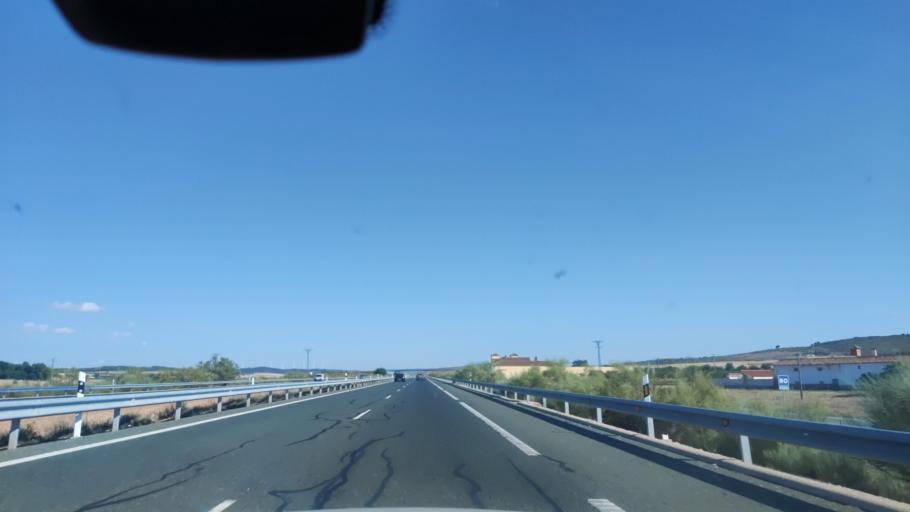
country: ES
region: Castille-La Mancha
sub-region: Provincia de Albacete
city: Pozo-Canada
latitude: 38.8384
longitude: -1.7597
